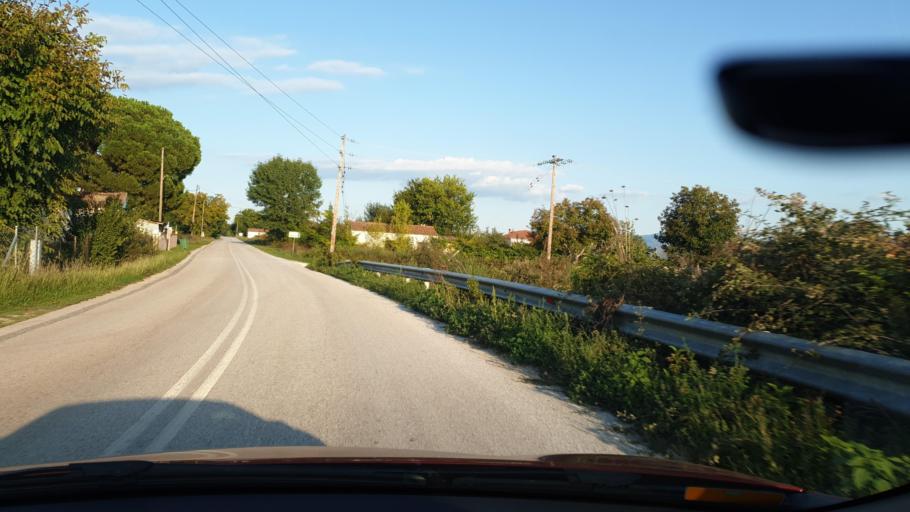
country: GR
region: Central Macedonia
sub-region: Nomos Thessalonikis
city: Nea Apollonia
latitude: 40.5543
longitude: 23.3618
